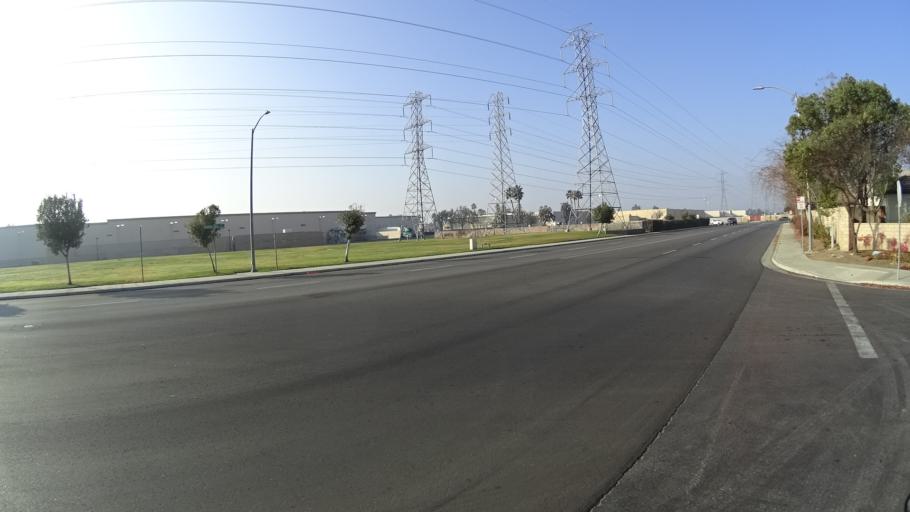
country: US
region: California
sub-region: Kern County
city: Greenacres
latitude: 35.3868
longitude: -119.0997
